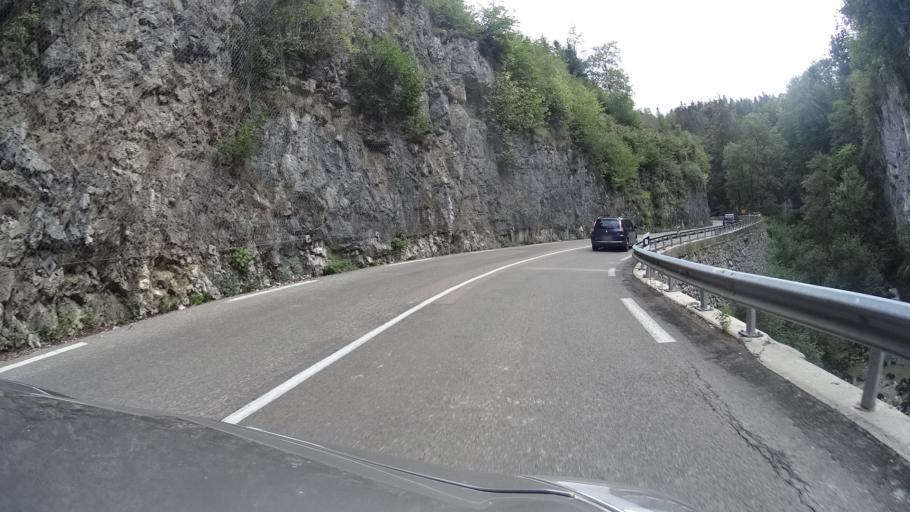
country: FR
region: Franche-Comte
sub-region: Departement du Jura
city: Champagnole
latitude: 46.6676
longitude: 5.9406
